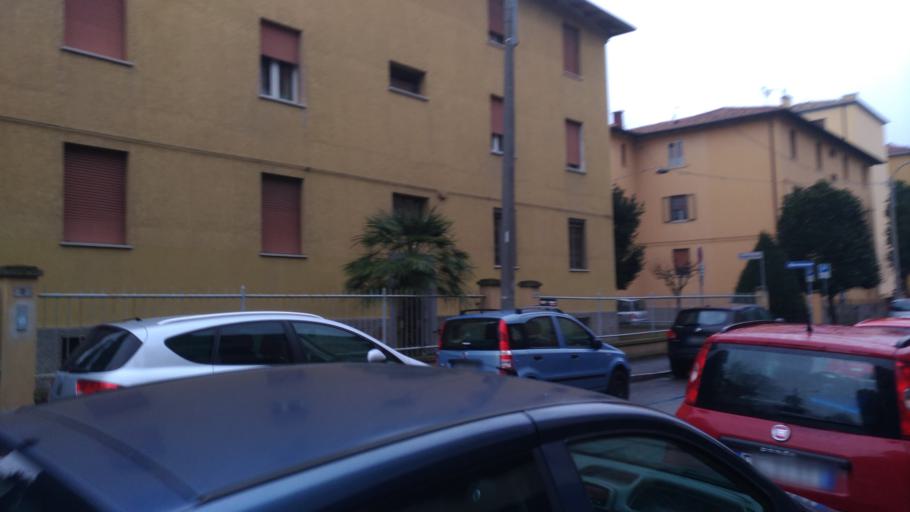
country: IT
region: Emilia-Romagna
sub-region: Provincia di Bologna
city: Bologna
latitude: 44.5247
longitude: 11.3489
